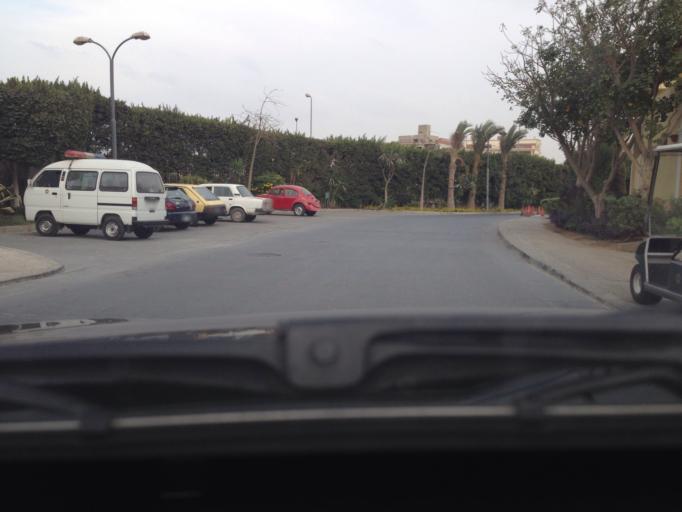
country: EG
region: Muhafazat al Qahirah
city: Cairo
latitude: 29.9987
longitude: 31.4051
